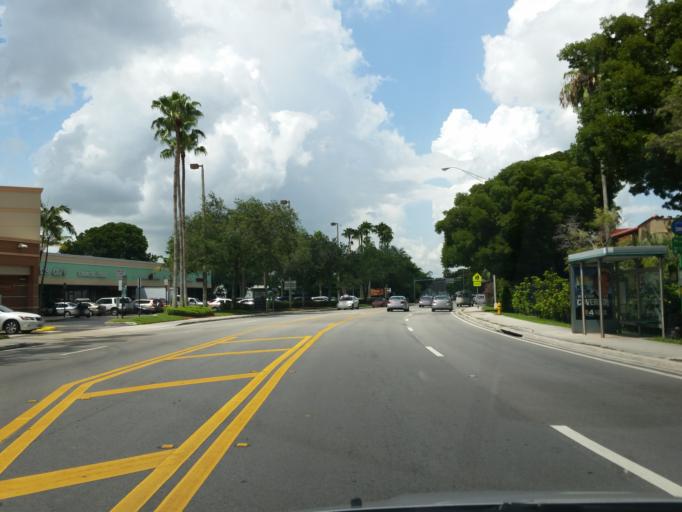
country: US
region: Florida
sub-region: Miami-Dade County
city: Sunset
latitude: 25.6851
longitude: -80.3662
